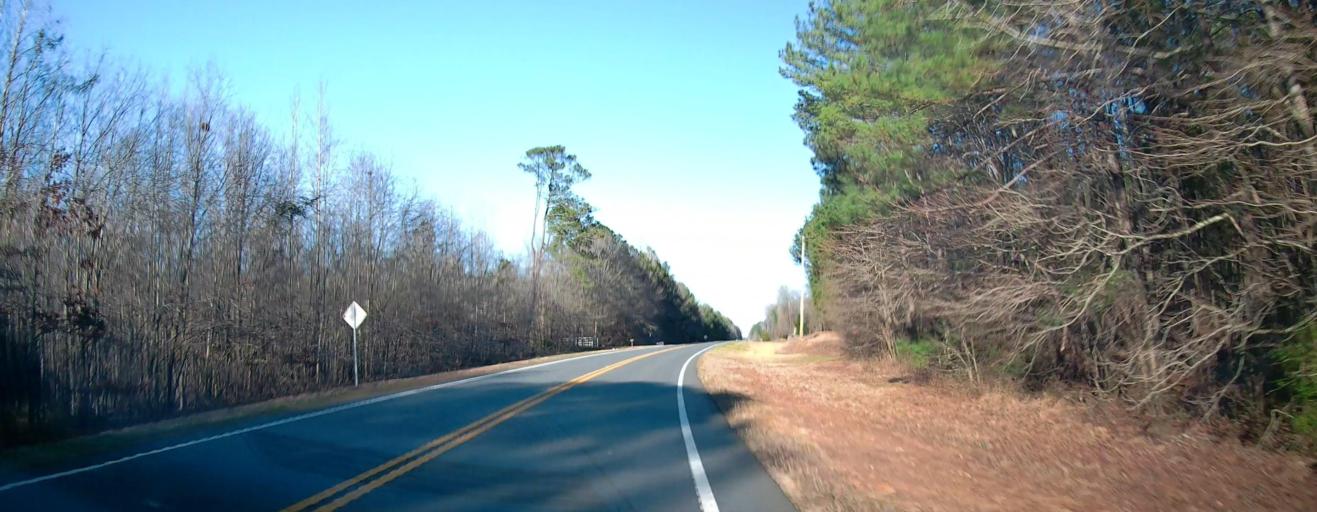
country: US
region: Georgia
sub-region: Meriwether County
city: Manchester
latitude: 32.9297
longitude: -84.6529
